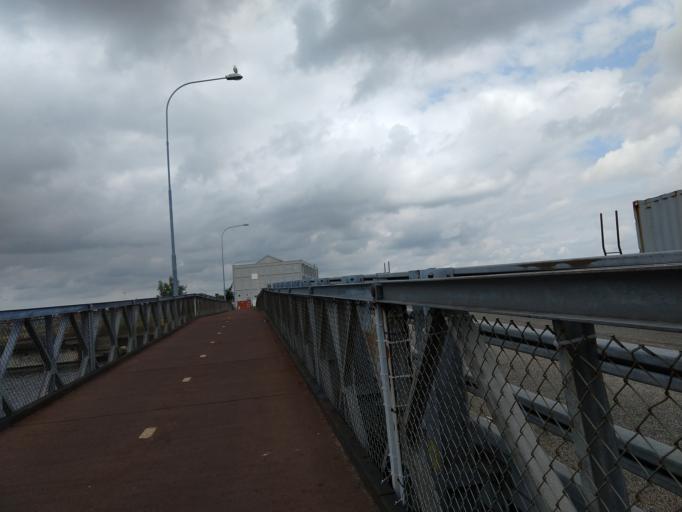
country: NL
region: Zeeland
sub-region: Gemeente Vlissingen
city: Vlissingen
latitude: 51.4443
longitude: 3.5815
